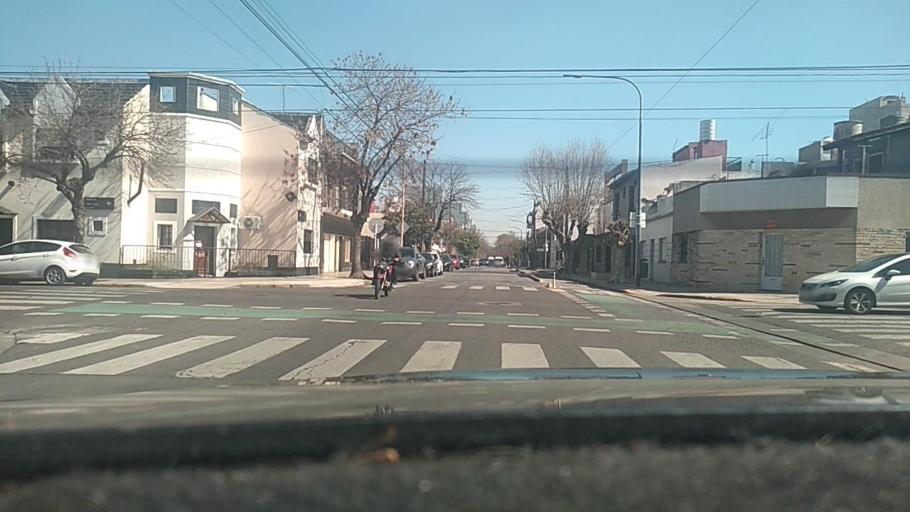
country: AR
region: Buenos Aires F.D.
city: Villa Santa Rita
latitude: -34.6113
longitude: -58.5014
